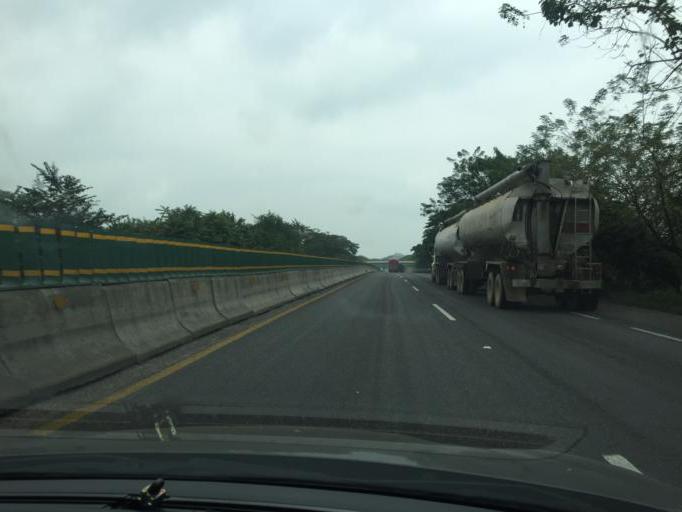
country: MX
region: Veracruz
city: Villa Nanchital
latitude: 18.0515
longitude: -94.3317
